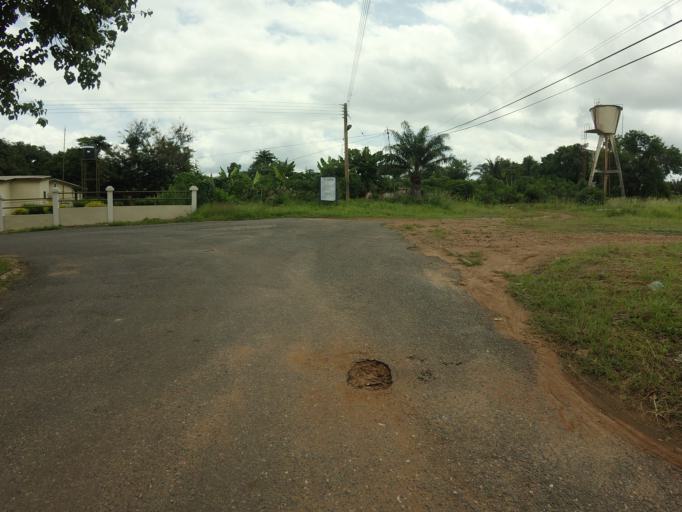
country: GH
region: Volta
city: Ho
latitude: 6.5916
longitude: 0.4672
